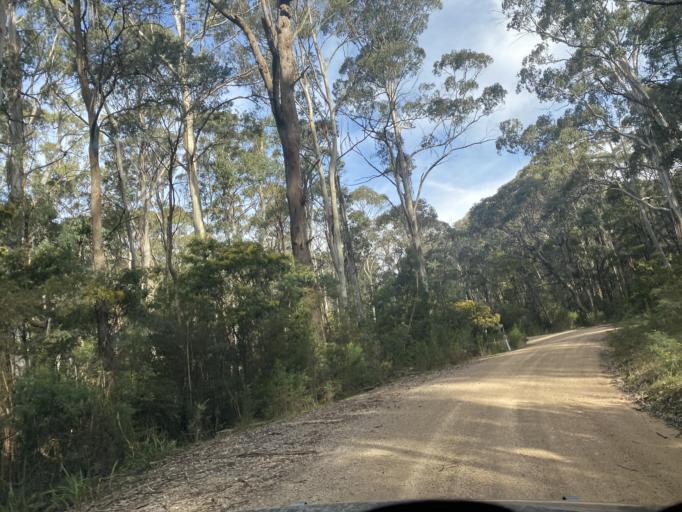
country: AU
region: Victoria
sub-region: Mansfield
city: Mansfield
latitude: -36.8640
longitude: 146.1978
